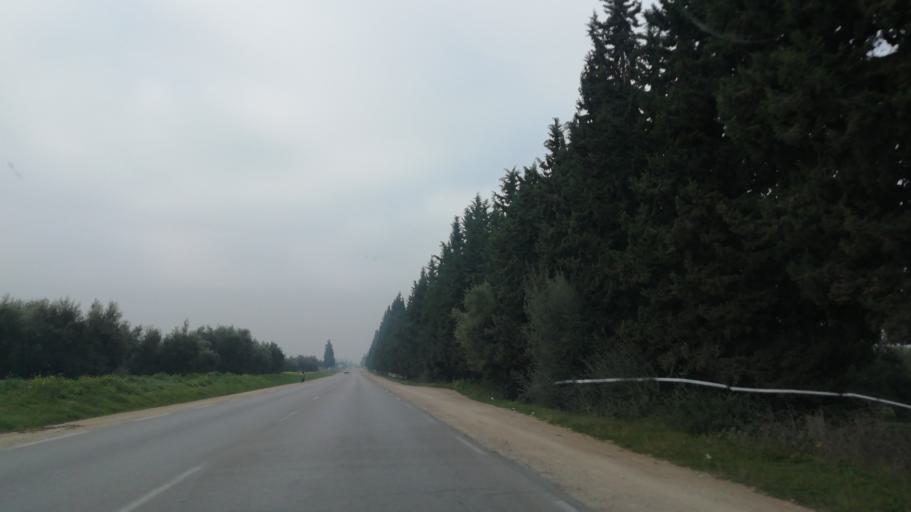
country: DZ
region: Relizane
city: Djidiouia
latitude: 35.9474
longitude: 0.8731
